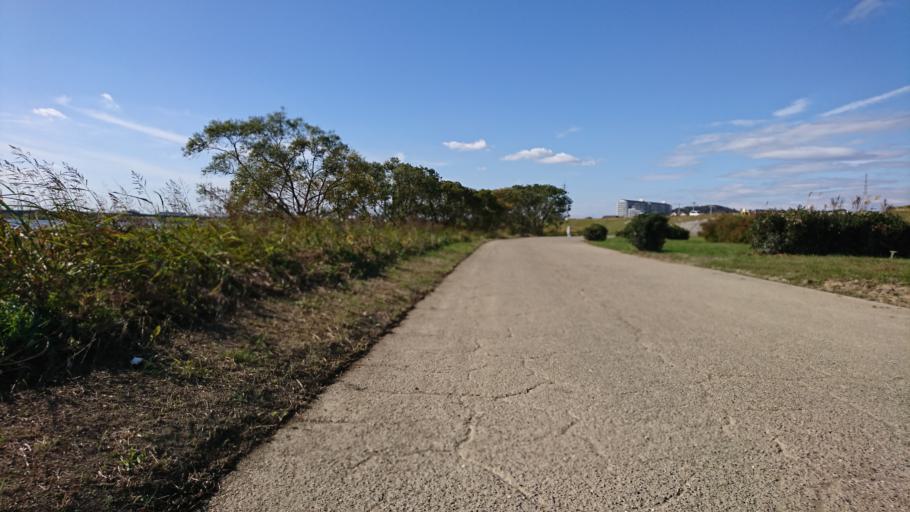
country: JP
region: Hyogo
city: Kakogawacho-honmachi
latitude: 34.7723
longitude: 134.8181
